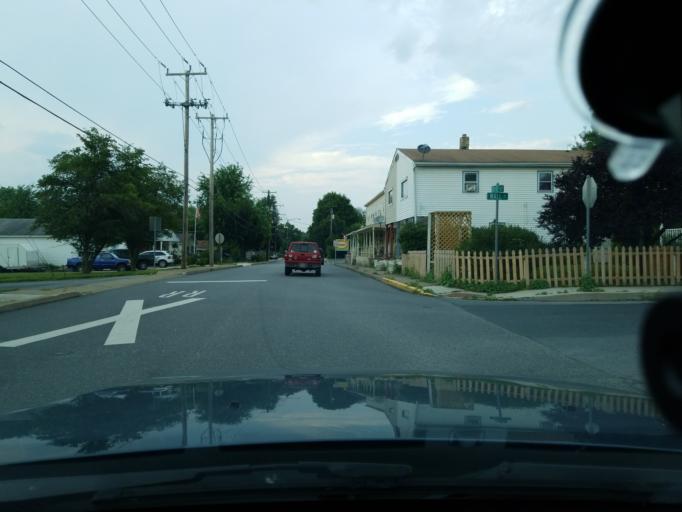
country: US
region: Pennsylvania
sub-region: Dauphin County
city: Hummelstown
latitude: 40.2674
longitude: -76.7173
